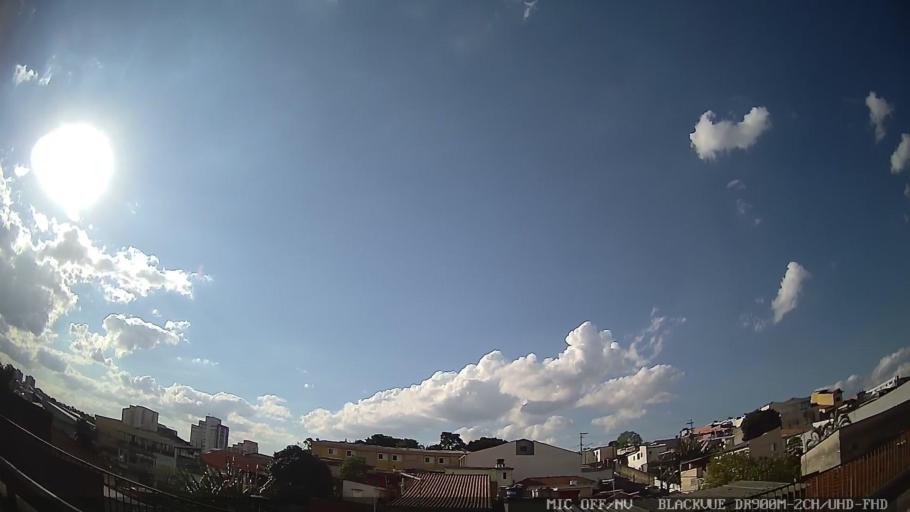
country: BR
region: Sao Paulo
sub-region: Ferraz De Vasconcelos
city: Ferraz de Vasconcelos
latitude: -23.5323
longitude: -46.4503
